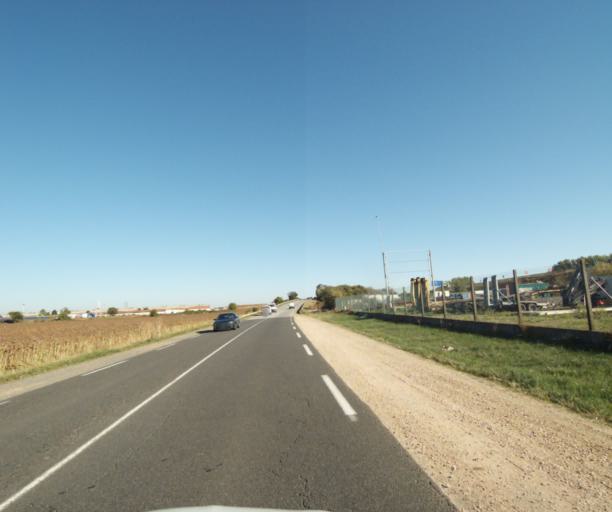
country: FR
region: Auvergne
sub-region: Departement du Puy-de-Dome
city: Aulnat
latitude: 45.8027
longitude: 3.1481
